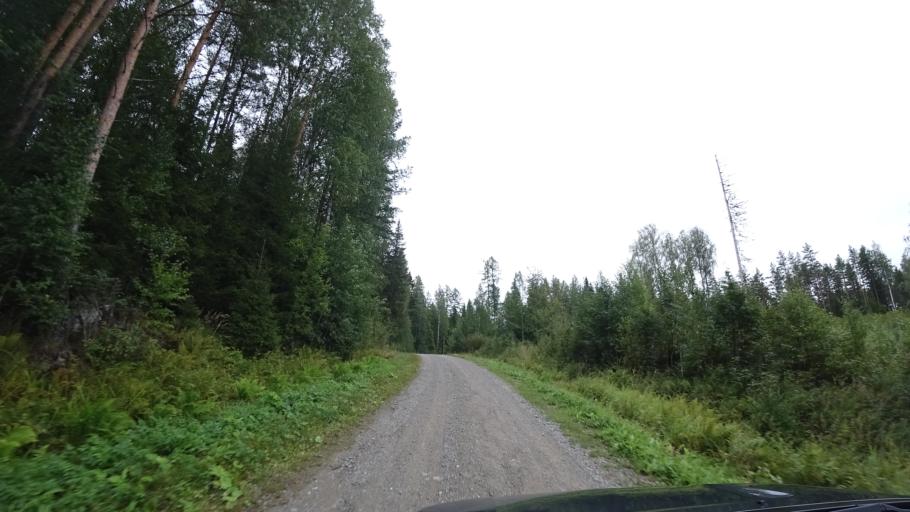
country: FI
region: Paijanne Tavastia
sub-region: Lahti
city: Auttoinen
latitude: 61.2205
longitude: 25.1474
